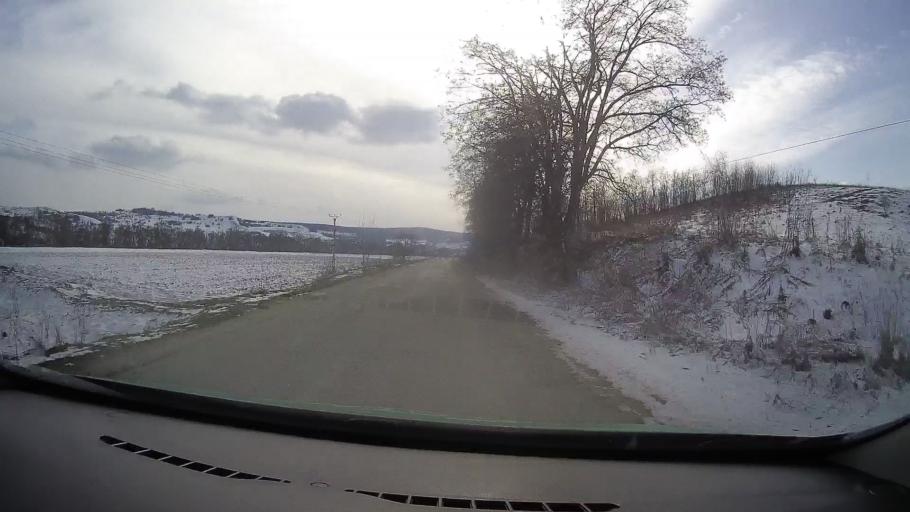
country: RO
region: Sibiu
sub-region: Comuna Iacobeni
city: Iacobeni
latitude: 46.0475
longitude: 24.7635
